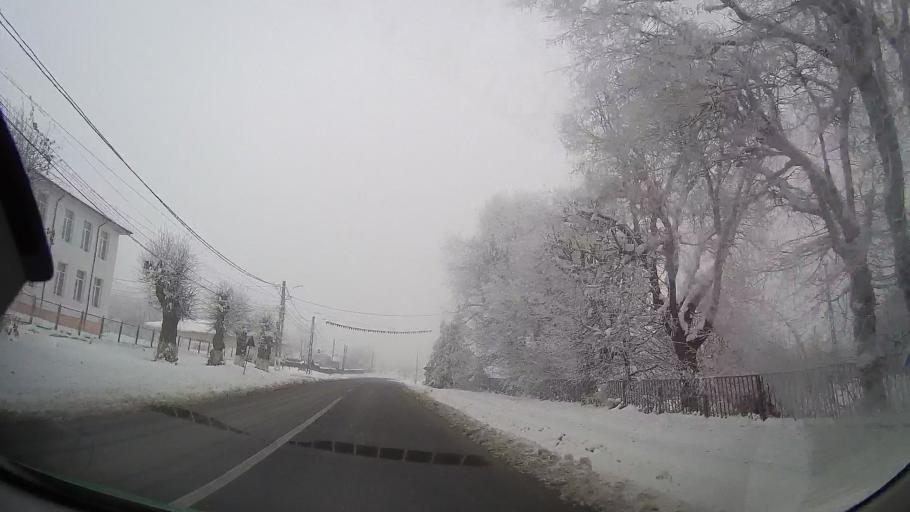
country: RO
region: Iasi
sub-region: Comuna Mogosesti-Siret
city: Mogosesti-Siret
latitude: 47.1663
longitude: 26.7686
